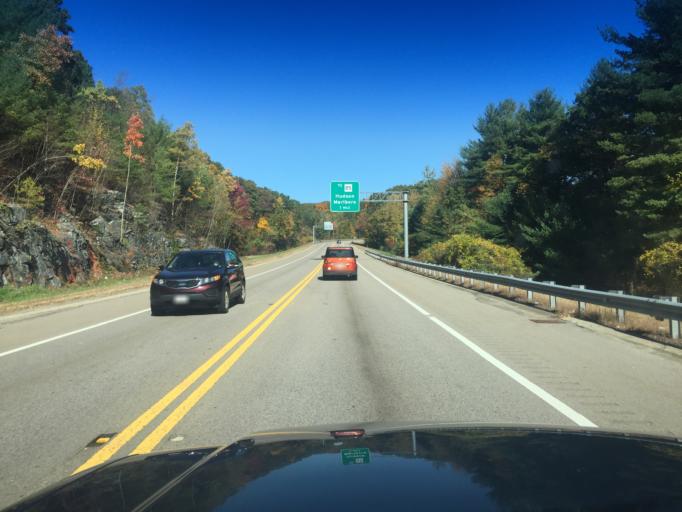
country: US
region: Massachusetts
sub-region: Middlesex County
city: Hudson
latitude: 42.3666
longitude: -71.5794
